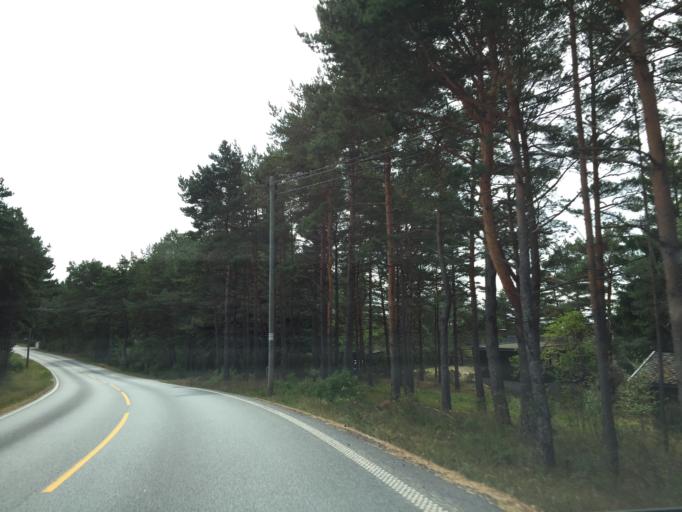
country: NO
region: Ostfold
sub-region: Hvaler
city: Skjaerhalden
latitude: 59.0706
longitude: 10.9338
